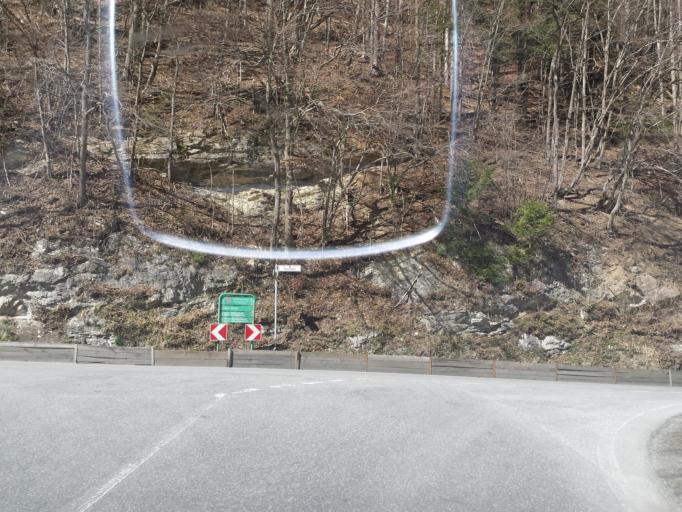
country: AT
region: Styria
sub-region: Politischer Bezirk Graz-Umgebung
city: Thal
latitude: 47.0795
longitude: 15.3653
